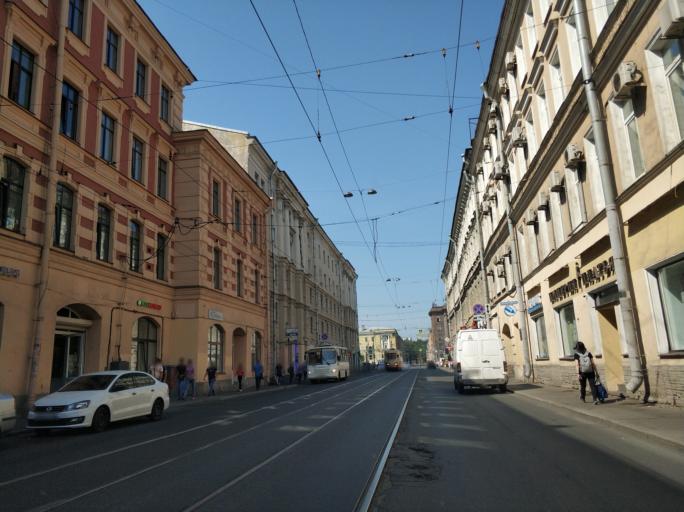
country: RU
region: Leningrad
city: Finlyandskiy
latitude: 59.9547
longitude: 30.3594
